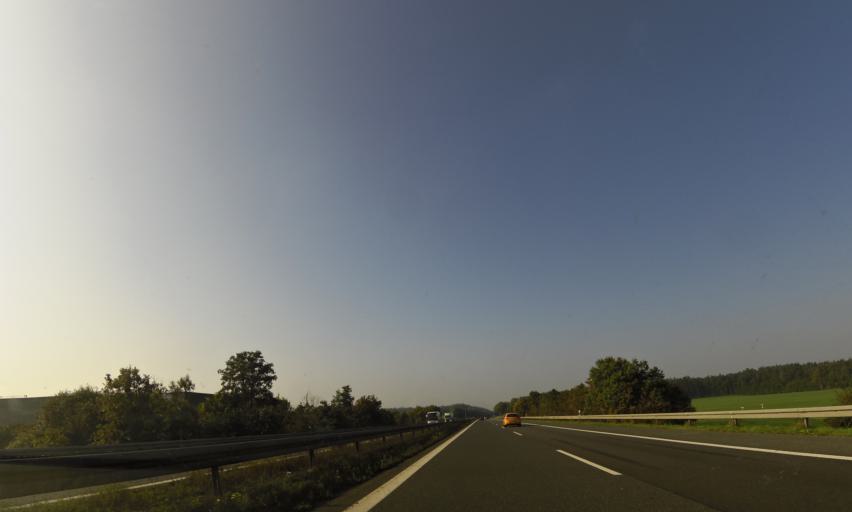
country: DE
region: Bavaria
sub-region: Regierungsbezirk Mittelfranken
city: Herrieden
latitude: 49.2577
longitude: 10.4962
